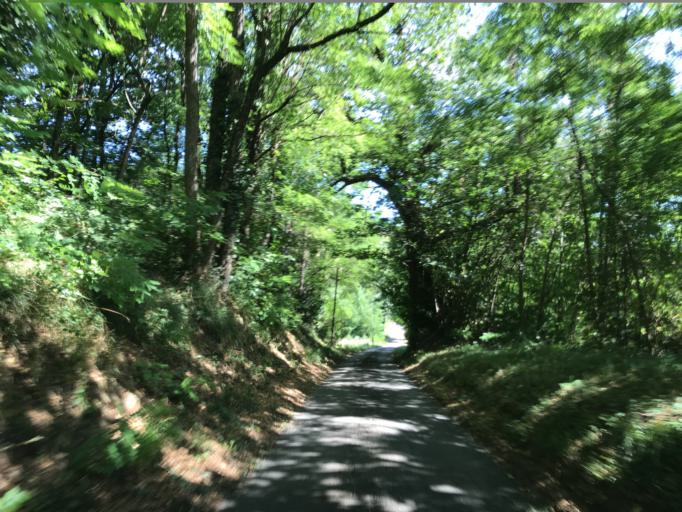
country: FR
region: Aquitaine
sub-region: Departement de la Dordogne
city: Sarlat-la-Caneda
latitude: 44.8968
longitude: 1.1970
